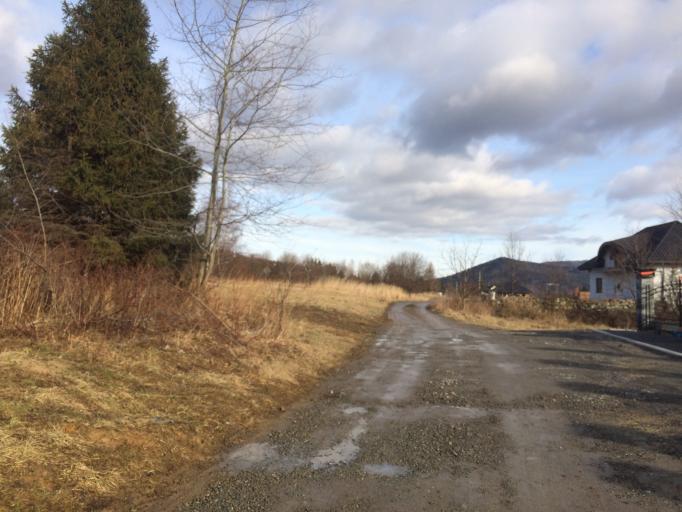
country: PL
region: Silesian Voivodeship
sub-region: Powiat bielski
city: Bystra
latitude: 49.7554
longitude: 19.0665
